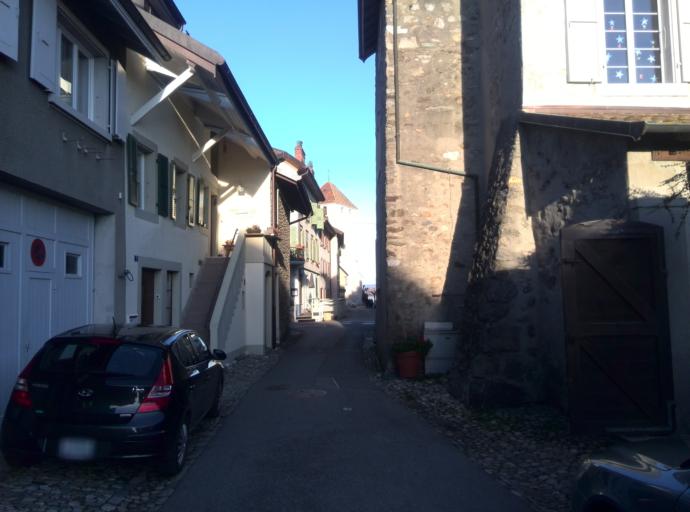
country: CH
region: Vaud
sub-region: Morges District
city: Saint-Prex
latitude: 46.4792
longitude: 6.4598
